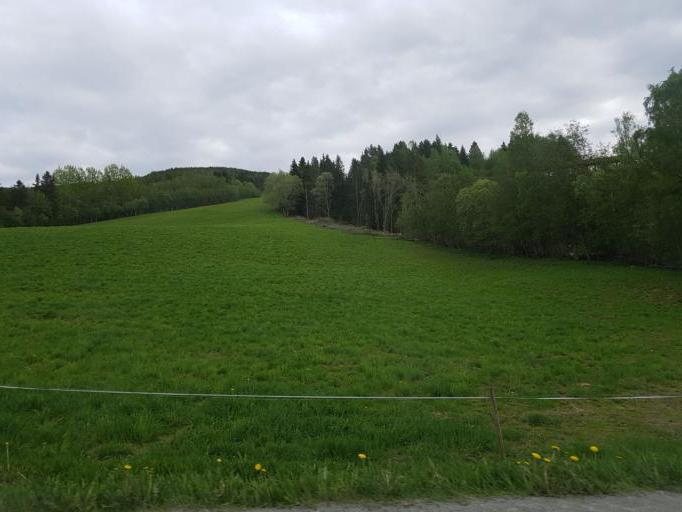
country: NO
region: Nord-Trondelag
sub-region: Levanger
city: Skogn
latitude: 63.6748
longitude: 11.2416
